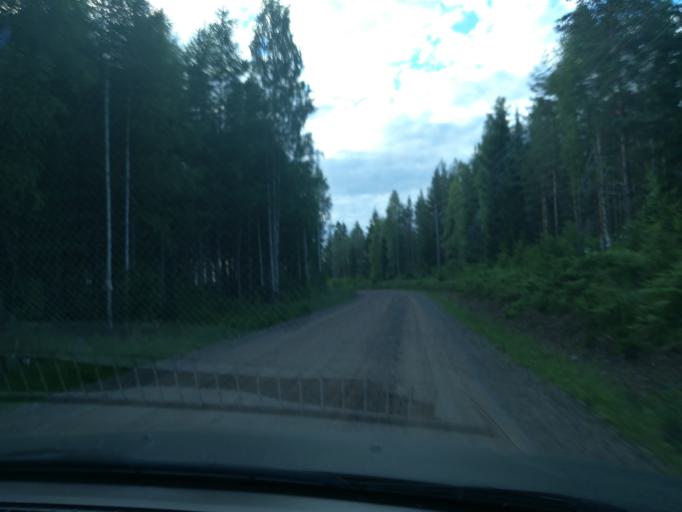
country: FI
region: Southern Savonia
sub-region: Mikkeli
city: Puumala
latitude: 61.6076
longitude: 28.1458
